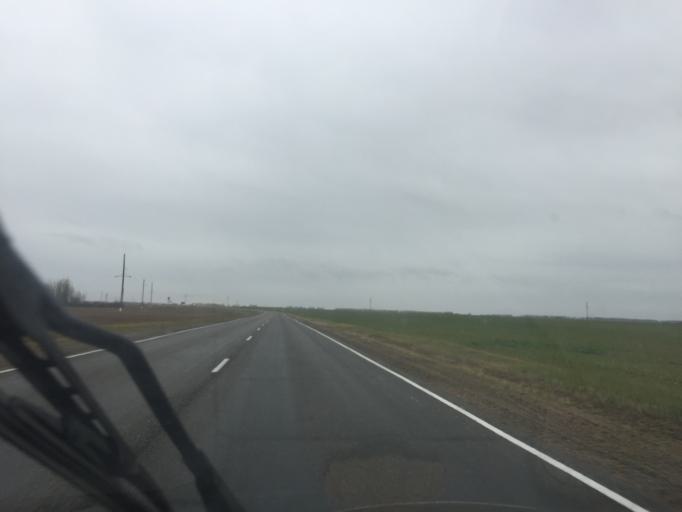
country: BY
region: Mogilev
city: Cherykaw
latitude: 53.5908
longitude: 31.3379
